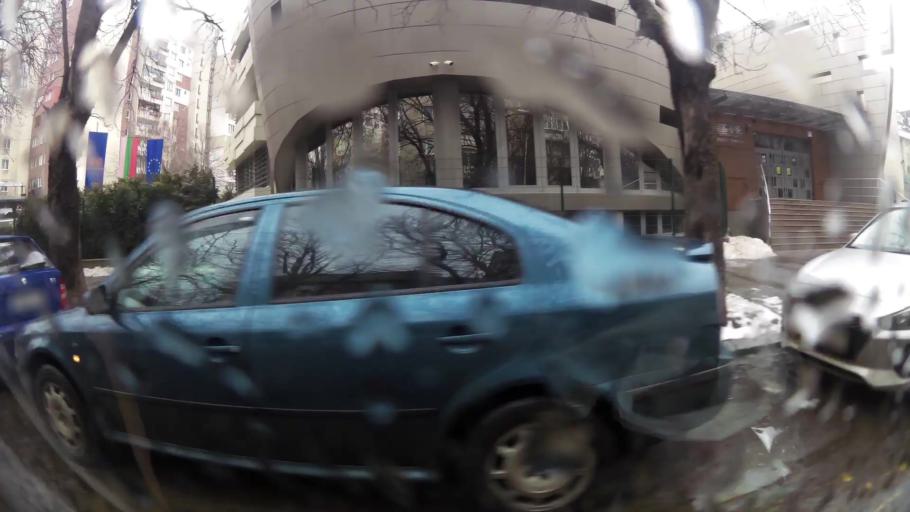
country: BG
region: Sofia-Capital
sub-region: Stolichna Obshtina
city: Sofia
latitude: 42.6761
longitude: 23.2941
